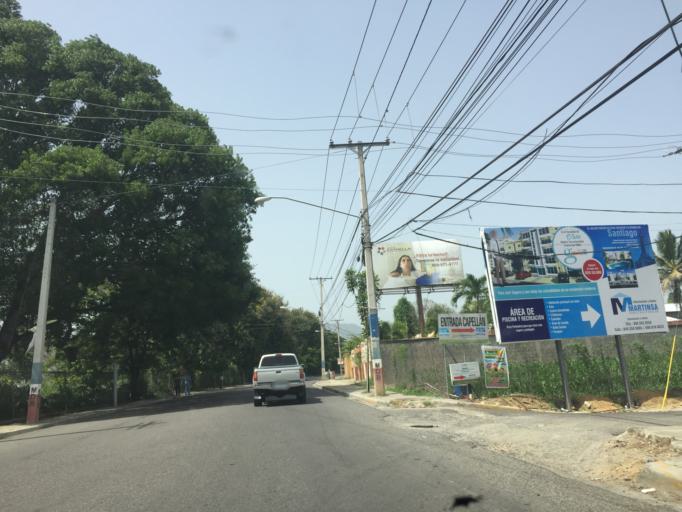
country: DO
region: Santiago
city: Tamboril
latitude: 19.4759
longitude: -70.6424
